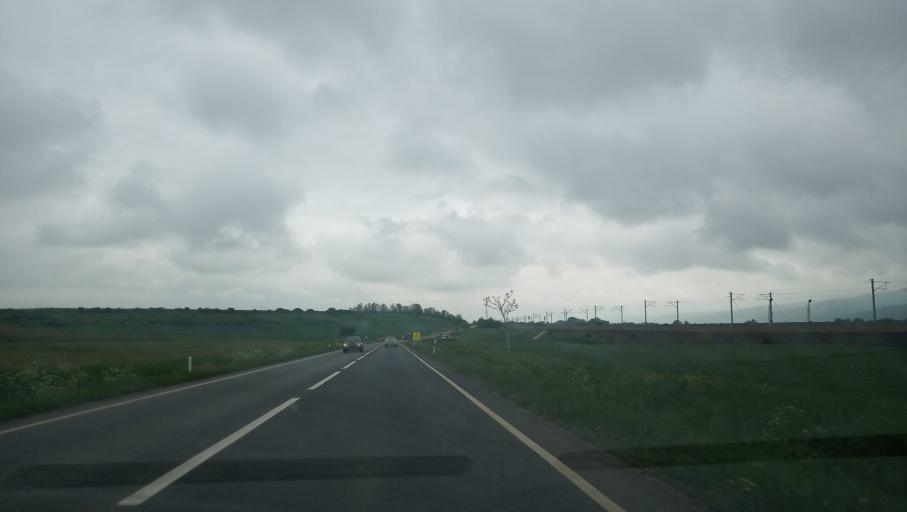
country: RO
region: Alba
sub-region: Comuna Blandiana
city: Blandiana
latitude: 45.9504
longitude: 23.4194
